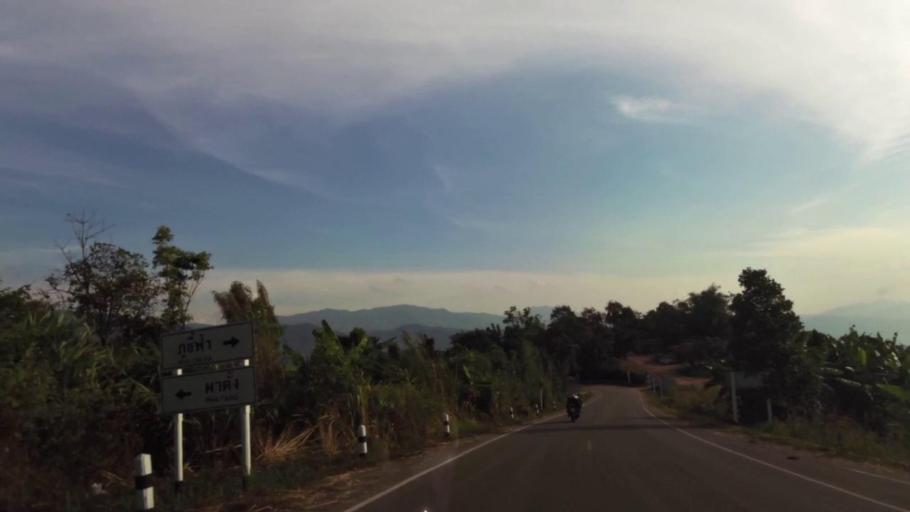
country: TH
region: Chiang Rai
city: Khun Tan
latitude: 19.8614
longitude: 100.3674
